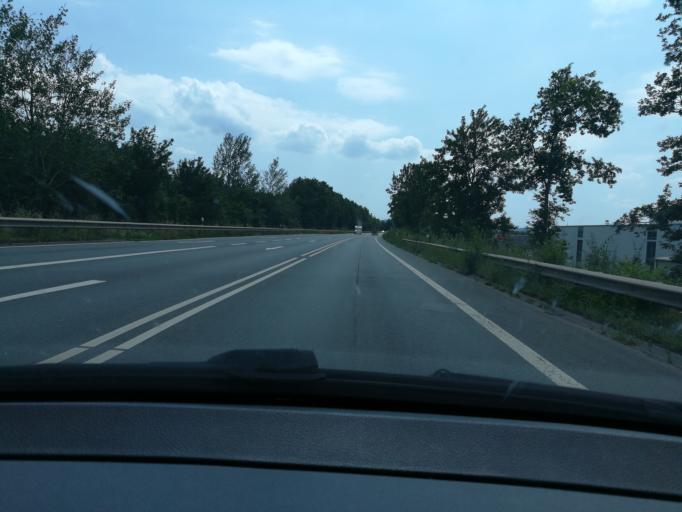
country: DE
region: North Rhine-Westphalia
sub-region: Regierungsbezirk Detmold
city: Petershagen
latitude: 52.3077
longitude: 8.9839
